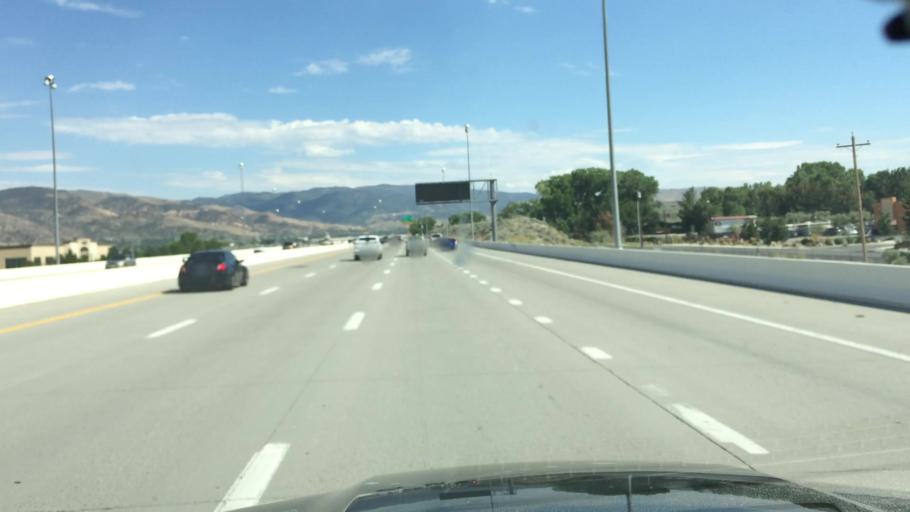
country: US
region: Nevada
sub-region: Washoe County
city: Sparks
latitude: 39.4286
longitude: -119.7578
